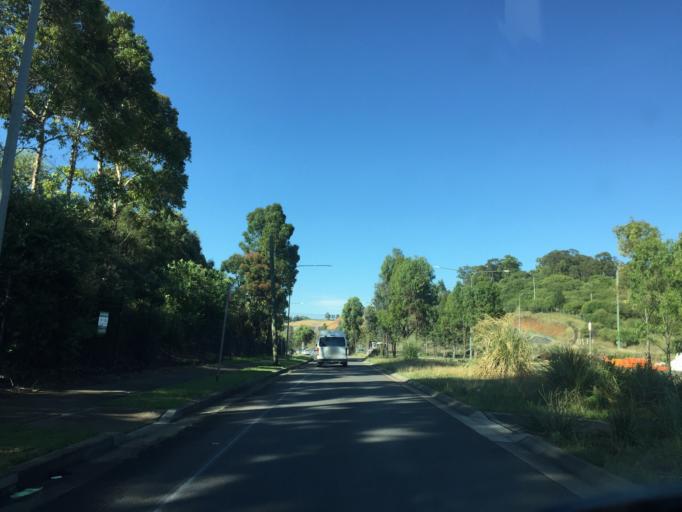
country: AU
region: New South Wales
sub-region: Holroyd
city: Girraween
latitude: -33.8177
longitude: 150.9199
